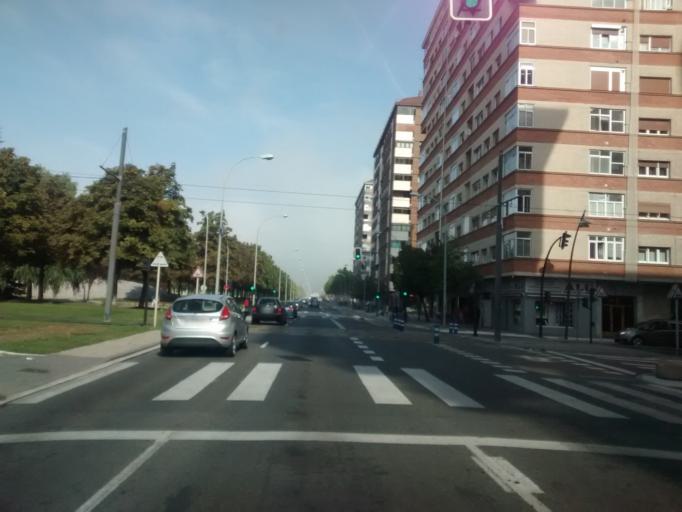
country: ES
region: Basque Country
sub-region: Provincia de Alava
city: Gasteiz / Vitoria
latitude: 42.8633
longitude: -2.6841
